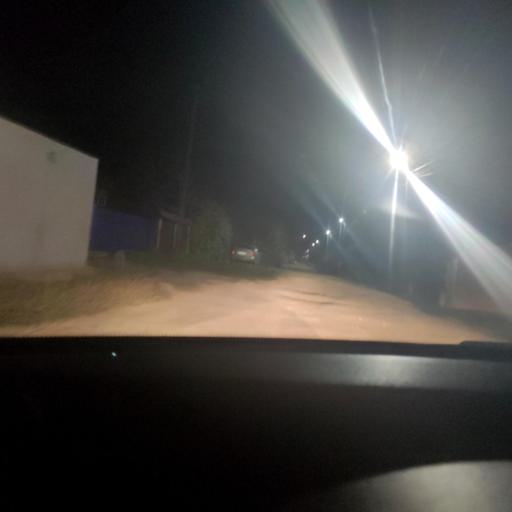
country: RU
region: Samara
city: Samara
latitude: 53.2249
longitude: 50.2178
